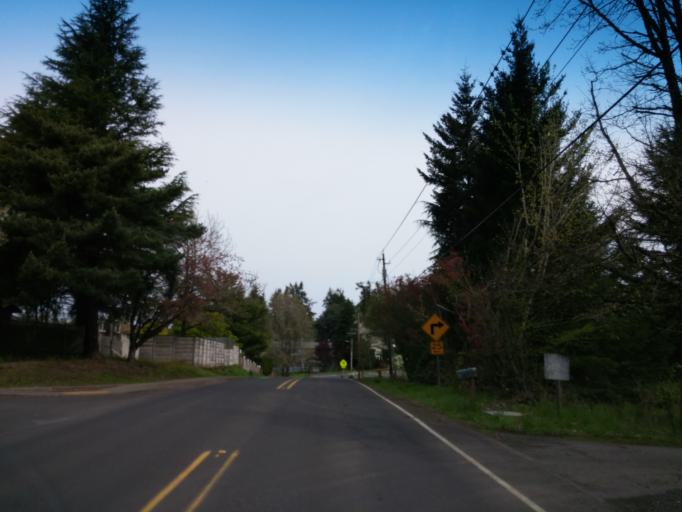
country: US
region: Oregon
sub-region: Washington County
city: Cedar Mill
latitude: 45.5372
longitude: -122.7995
